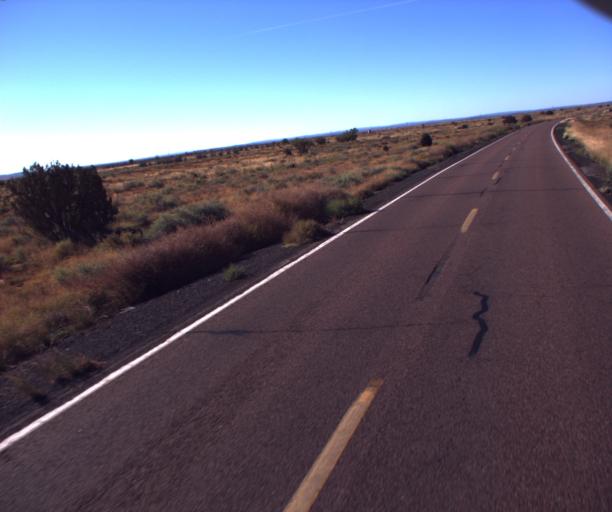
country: US
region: Arizona
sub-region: Navajo County
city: Heber-Overgaard
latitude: 34.6309
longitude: -110.3619
